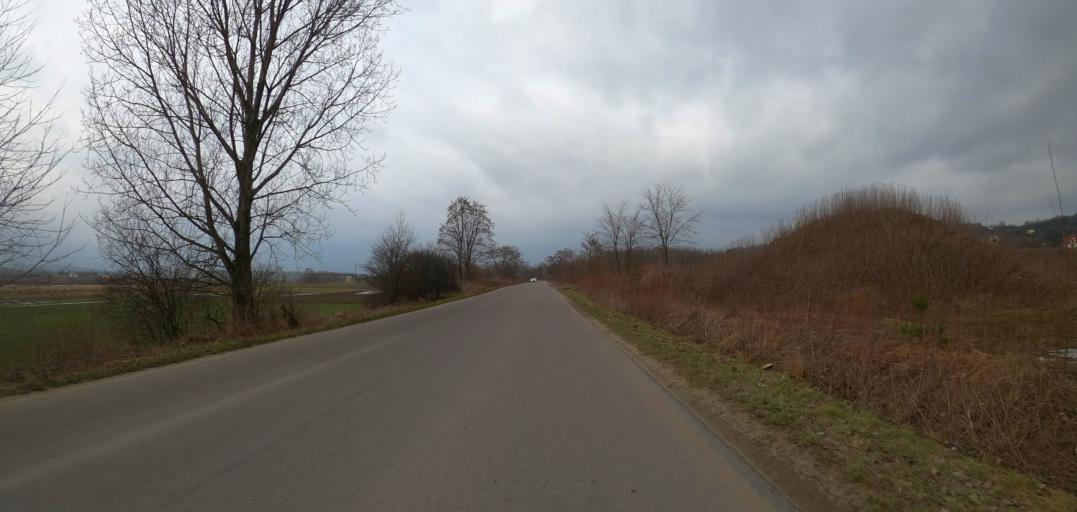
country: PL
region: Subcarpathian Voivodeship
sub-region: Powiat debicki
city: Pilzno
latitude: 49.9825
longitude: 21.3287
